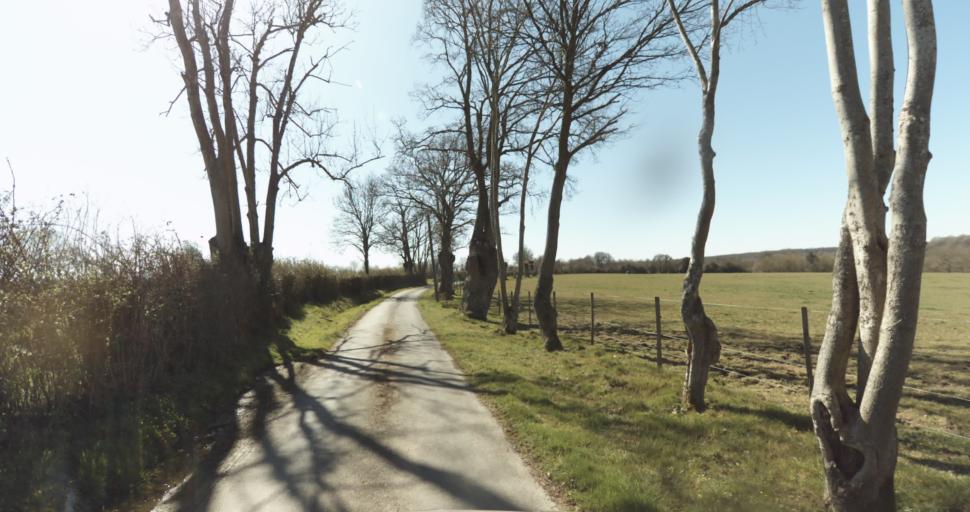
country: FR
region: Lower Normandy
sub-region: Departement du Calvados
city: Livarot
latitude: 48.9870
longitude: 0.1026
